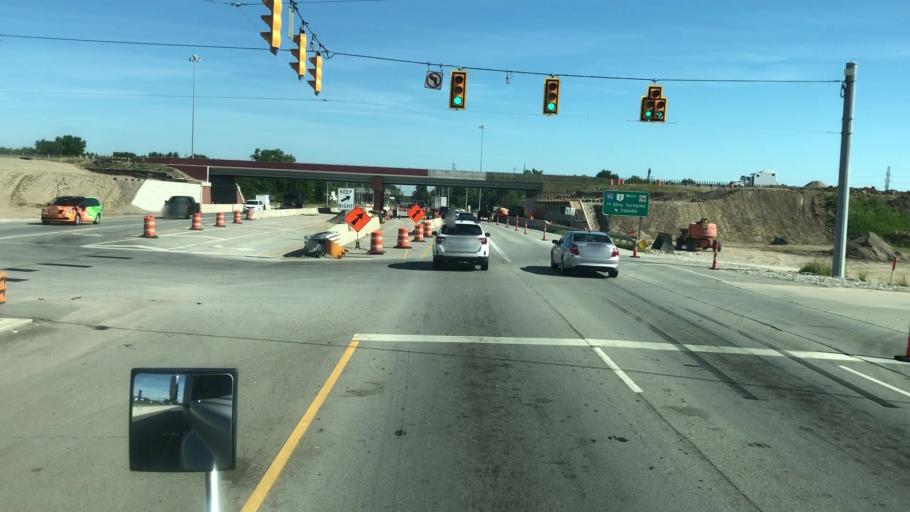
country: US
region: Ohio
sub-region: Lorain County
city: Sheffield
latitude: 41.4036
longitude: -82.1168
